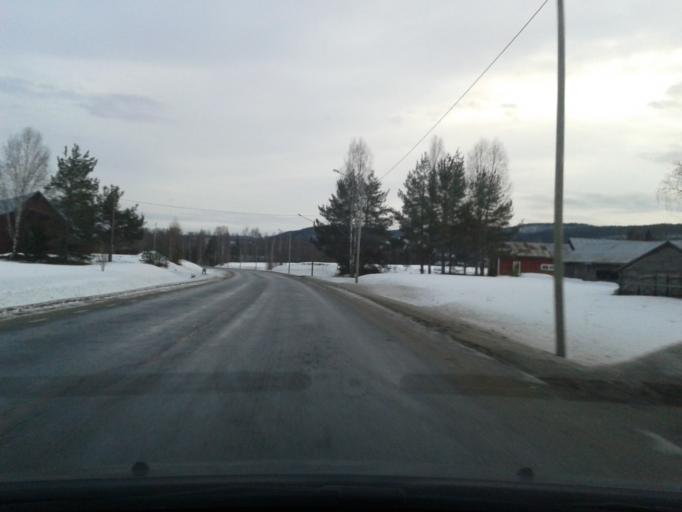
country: SE
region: Vaesternorrland
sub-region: Solleftea Kommun
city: Solleftea
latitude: 63.2456
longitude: 17.2083
